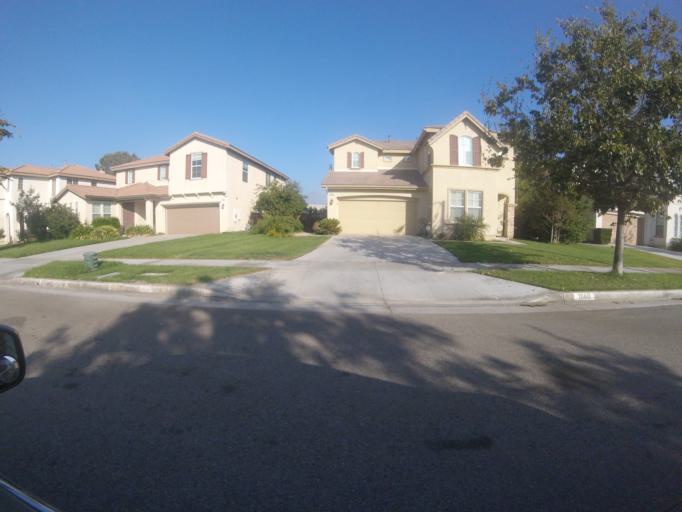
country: US
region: California
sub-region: San Bernardino County
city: Redlands
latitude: 34.0823
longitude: -117.1862
